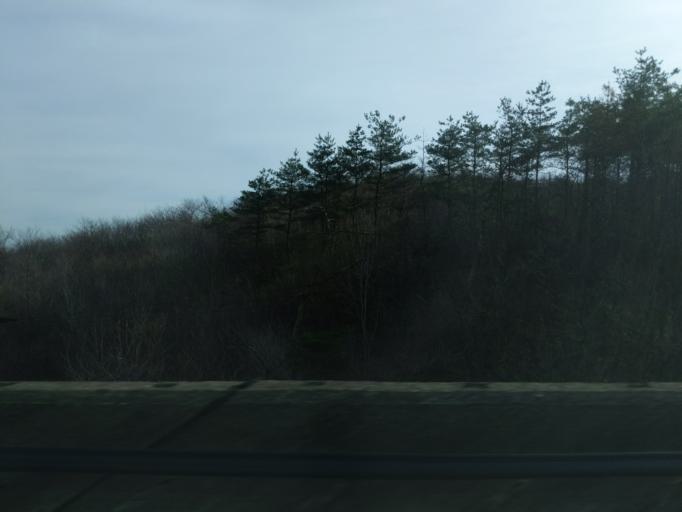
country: JP
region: Miyagi
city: Kogota
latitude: 38.6903
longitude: 141.0386
